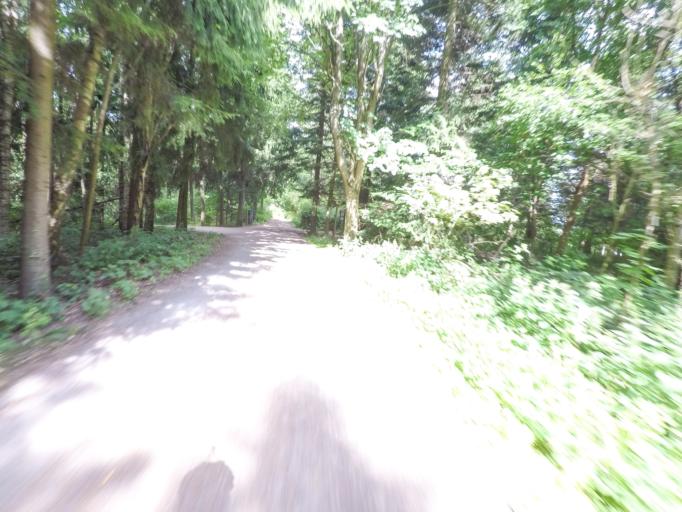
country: FI
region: Uusimaa
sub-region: Helsinki
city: Vantaa
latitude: 60.2176
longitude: 25.0089
